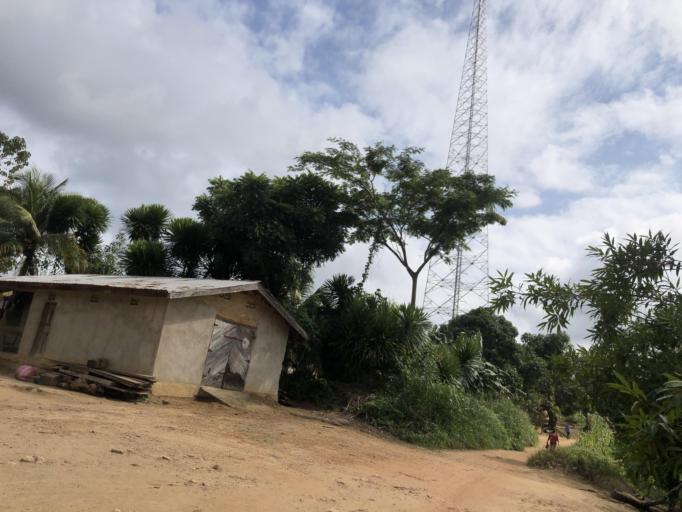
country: SL
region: Eastern Province
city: Kailahun
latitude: 8.2843
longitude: -10.5647
